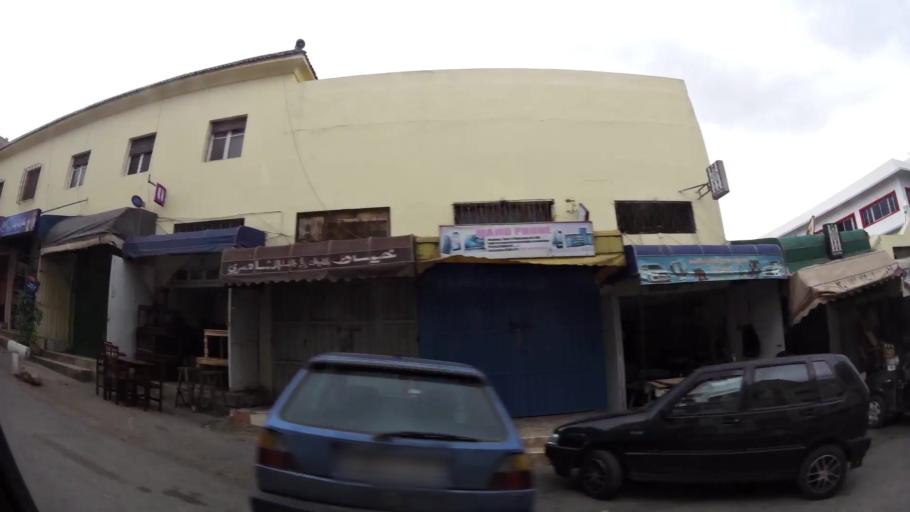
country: MA
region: Grand Casablanca
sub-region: Mediouna
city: Tit Mellil
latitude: 33.5702
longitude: -7.5394
